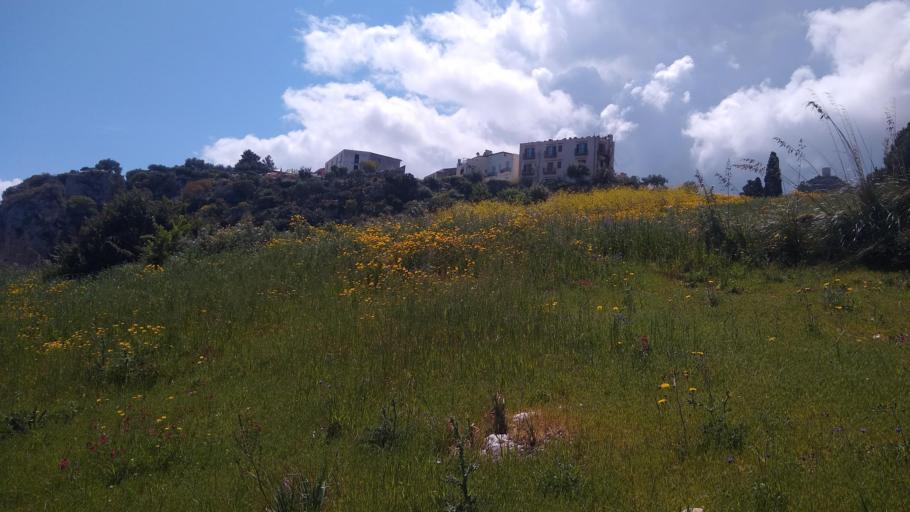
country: IT
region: Sicily
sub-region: Trapani
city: Castelluzzo
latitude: 38.0725
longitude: 12.8188
